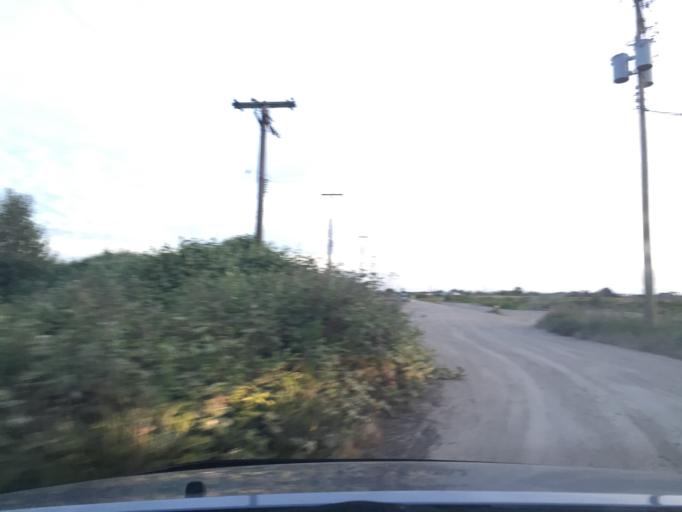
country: CA
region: British Columbia
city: Ladner
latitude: 49.1467
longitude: -123.0467
